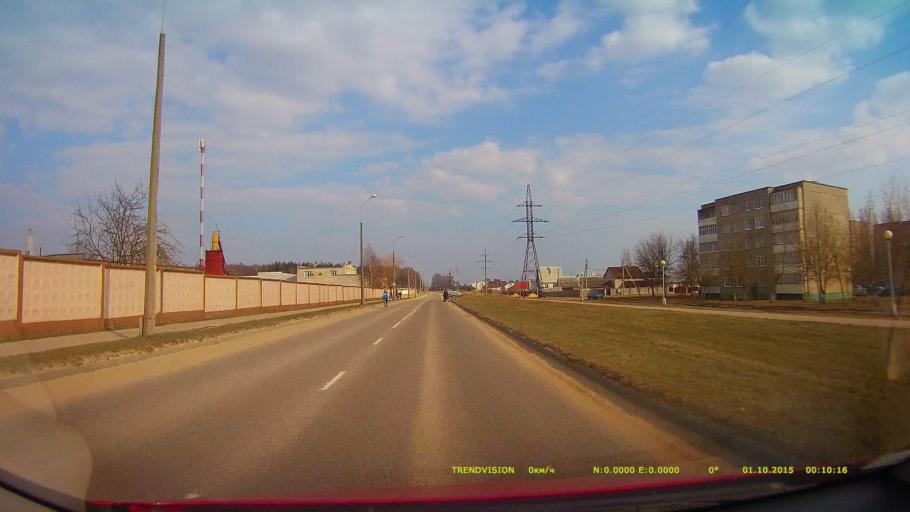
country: BY
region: Grodnenskaya
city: Lida
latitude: 53.9361
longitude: 25.2683
